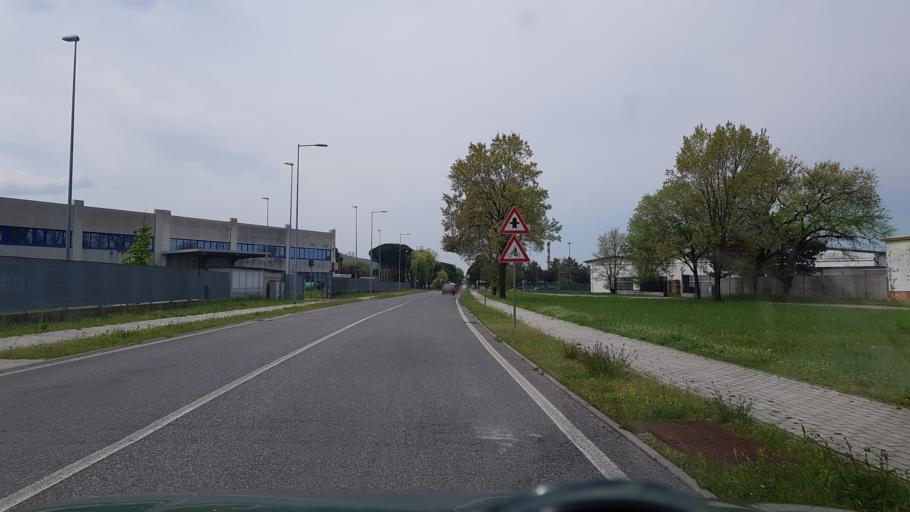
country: IT
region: Friuli Venezia Giulia
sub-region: Provincia di Gorizia
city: Savogna d'Isonzo
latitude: 45.9145
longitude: 13.5930
